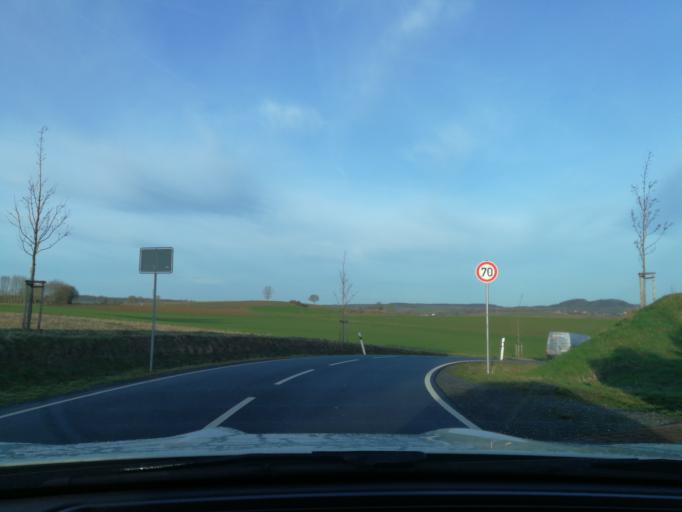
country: DE
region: Hesse
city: Reinheim
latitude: 49.8326
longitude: 8.8246
